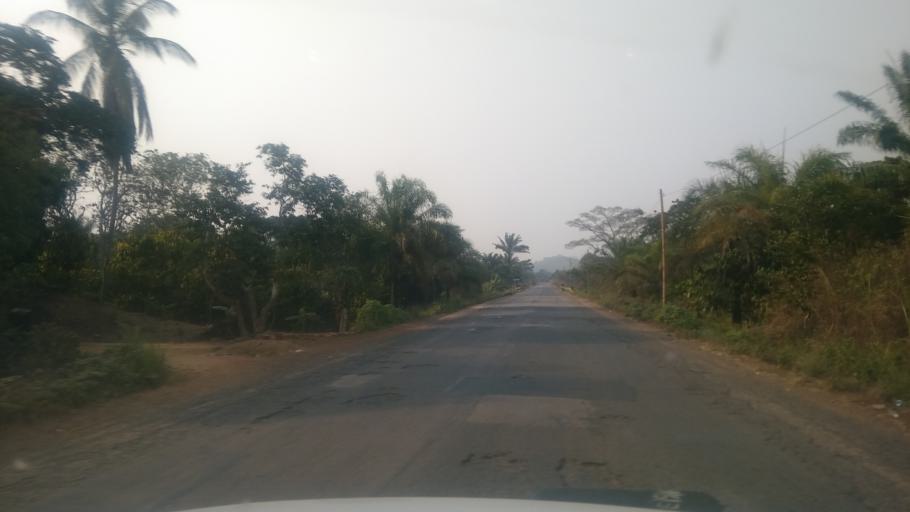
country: CM
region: West
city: Tonga
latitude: 4.9960
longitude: 10.7009
